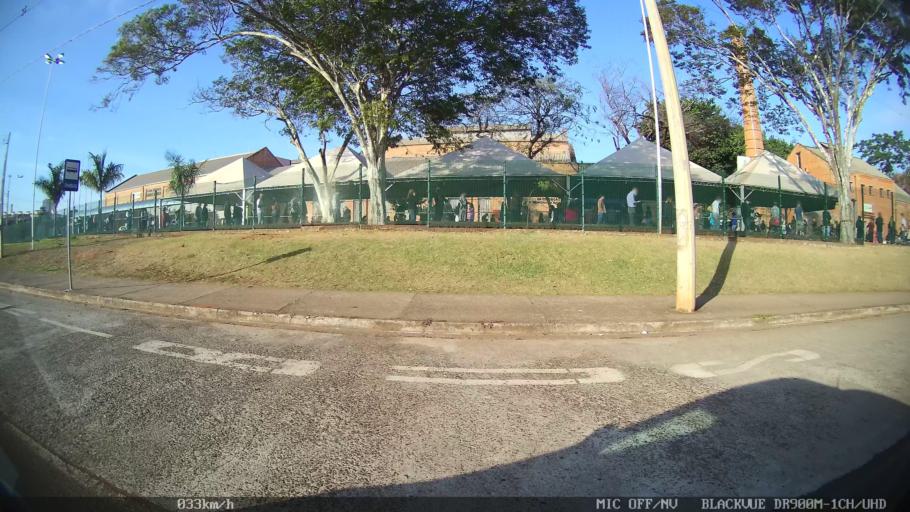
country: BR
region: Sao Paulo
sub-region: Sao Jose Do Rio Preto
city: Sao Jose do Rio Preto
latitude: -20.8101
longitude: -49.3691
